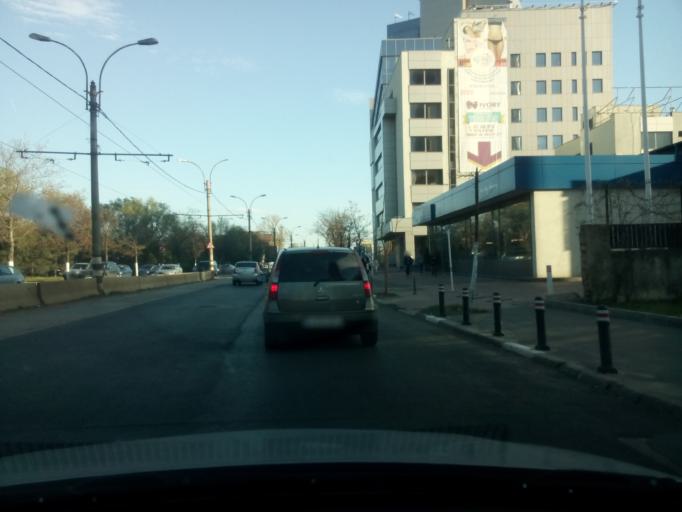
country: RO
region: Bucuresti
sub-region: Municipiul Bucuresti
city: Bucharest
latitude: 44.4772
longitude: 26.1058
